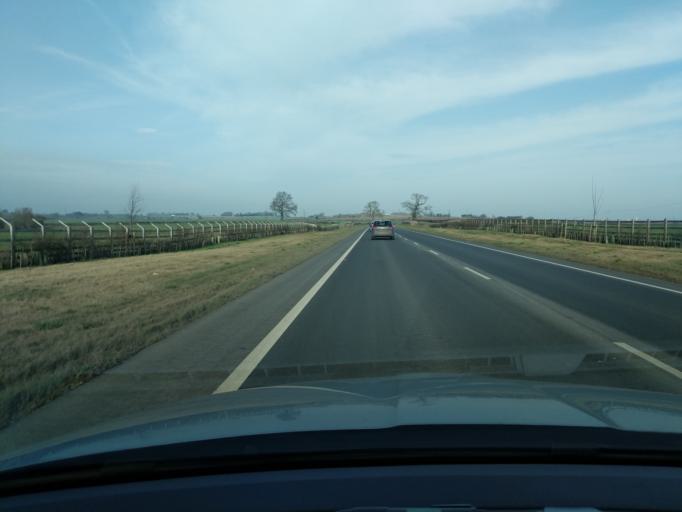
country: GB
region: England
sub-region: North Yorkshire
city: Bedale
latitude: 54.3047
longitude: -1.5834
